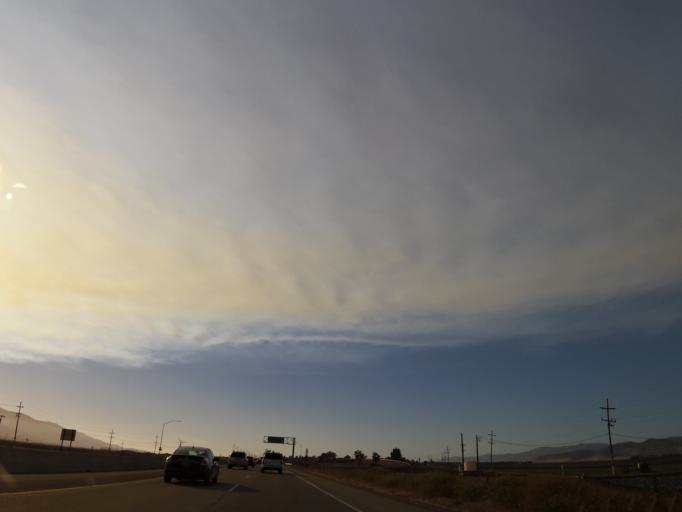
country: US
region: California
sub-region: Monterey County
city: Gonzales
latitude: 36.4879
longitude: -121.4224
